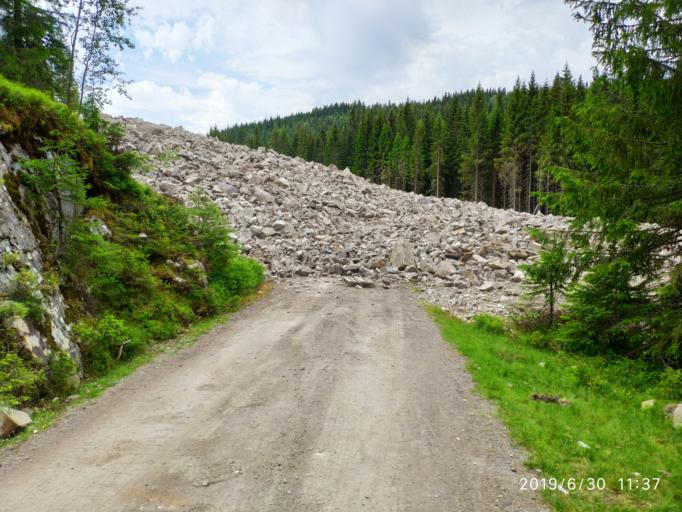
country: NO
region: Oppland
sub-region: Lunner
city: Grua
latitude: 60.2698
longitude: 10.7606
